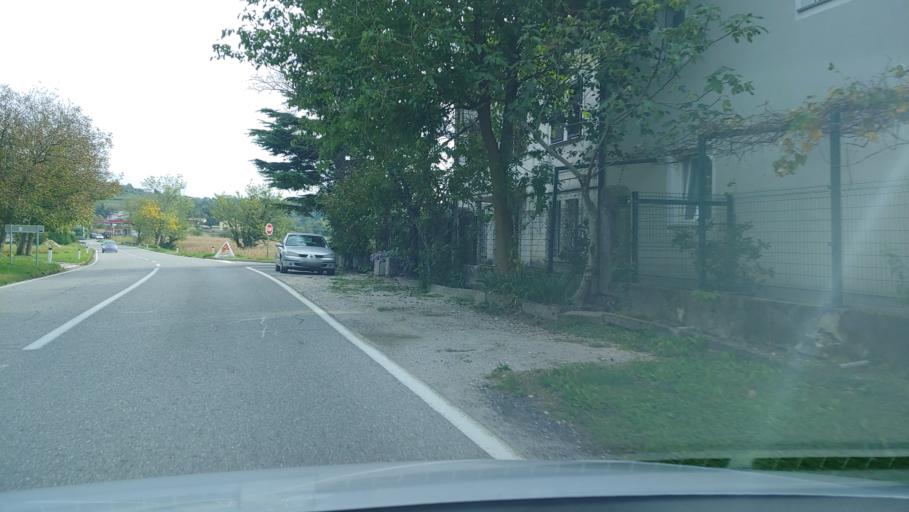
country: SI
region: Nova Gorica
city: Sempas
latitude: 45.9322
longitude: 13.7379
